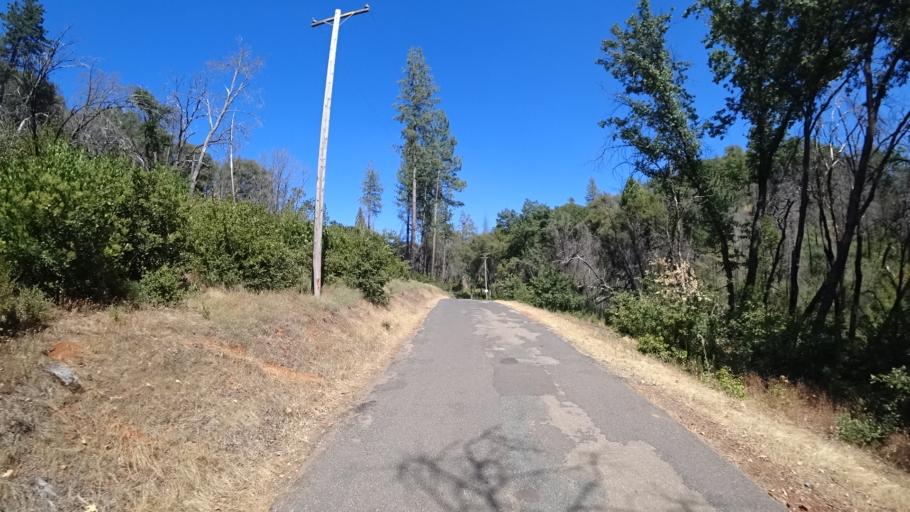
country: US
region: California
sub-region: Calaveras County
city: Mountain Ranch
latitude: 38.2863
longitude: -120.5819
